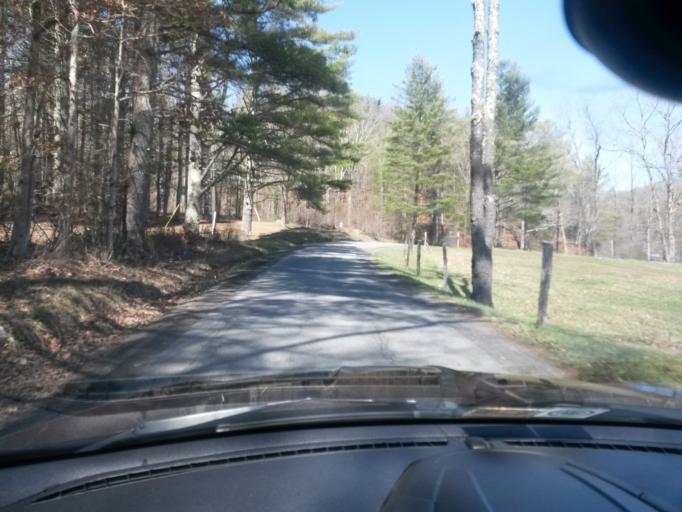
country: US
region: West Virginia
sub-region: Greenbrier County
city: White Sulphur Springs
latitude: 37.6510
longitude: -80.3267
